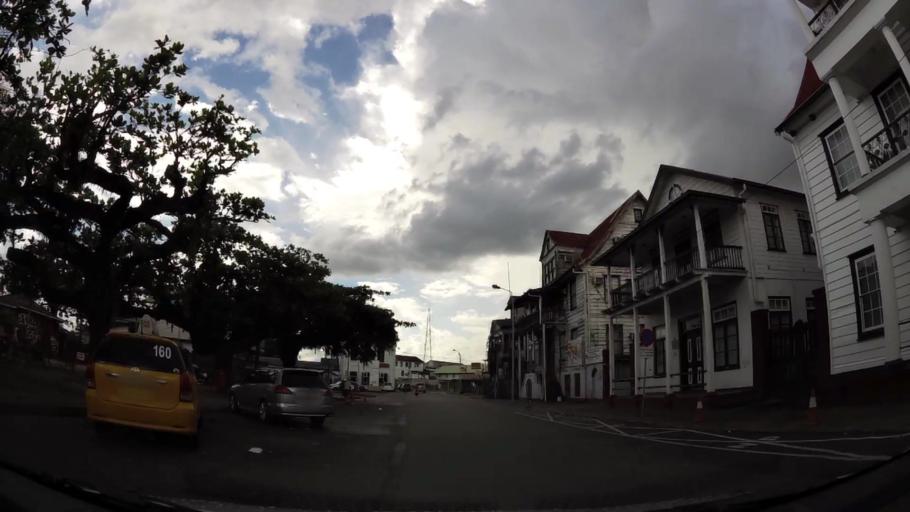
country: SR
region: Paramaribo
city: Paramaribo
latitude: 5.8252
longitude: -55.1534
